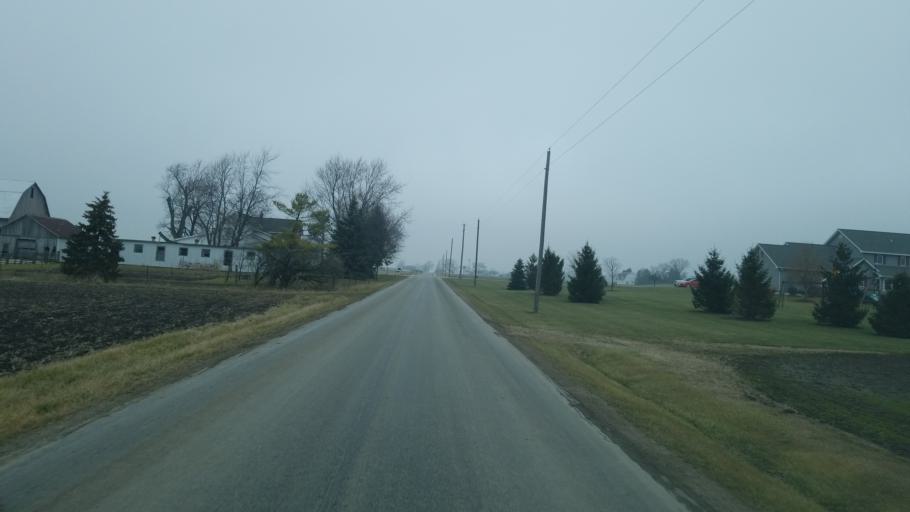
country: US
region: Indiana
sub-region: Adams County
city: Berne
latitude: 40.7138
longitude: -84.9751
